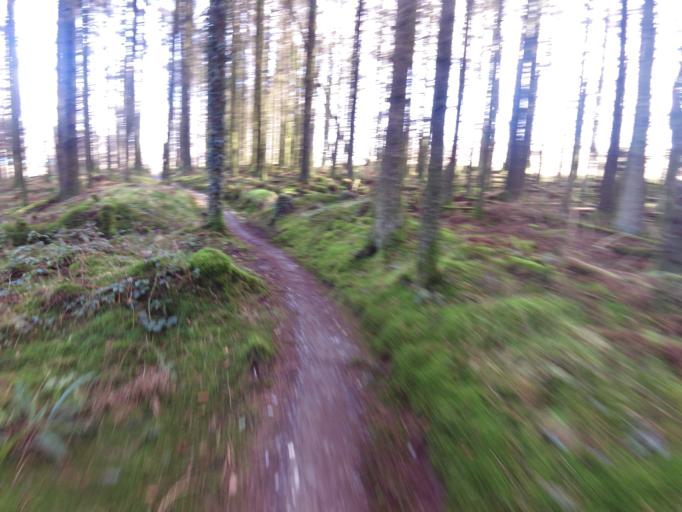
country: GB
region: Wales
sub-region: County of Ceredigion
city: Bow Street
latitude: 52.4353
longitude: -3.8985
